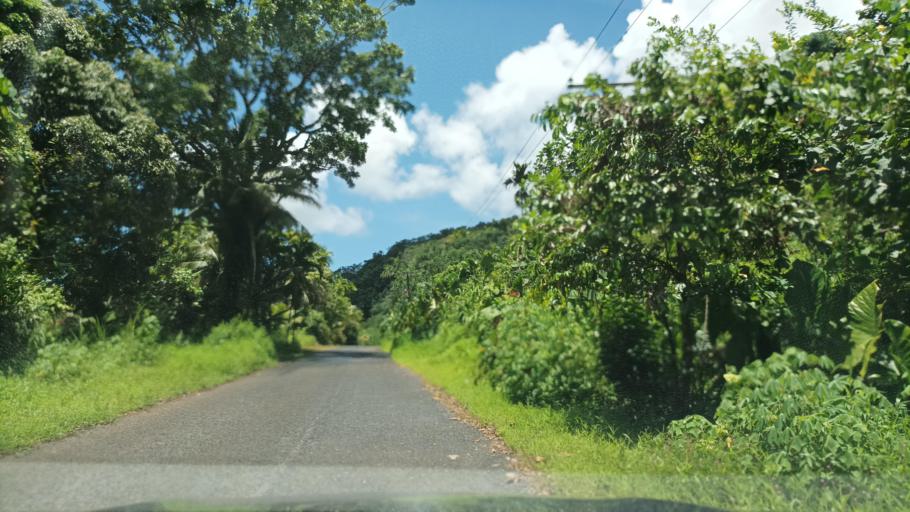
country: FM
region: Pohnpei
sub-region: Madolenihm Municipality
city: Madolenihm Municipality Government
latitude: 6.8648
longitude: 158.2914
